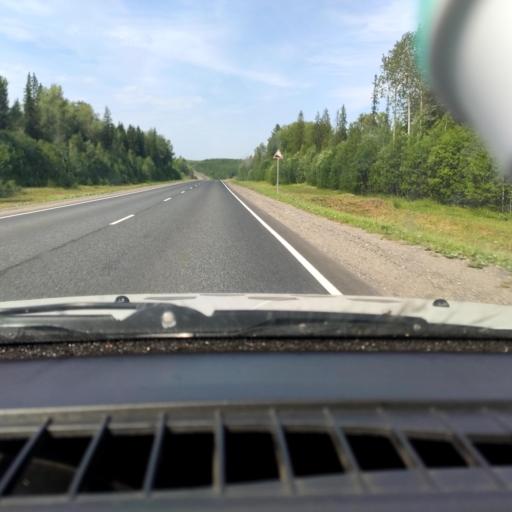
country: RU
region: Kirov
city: Kostino
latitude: 58.7639
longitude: 53.6098
